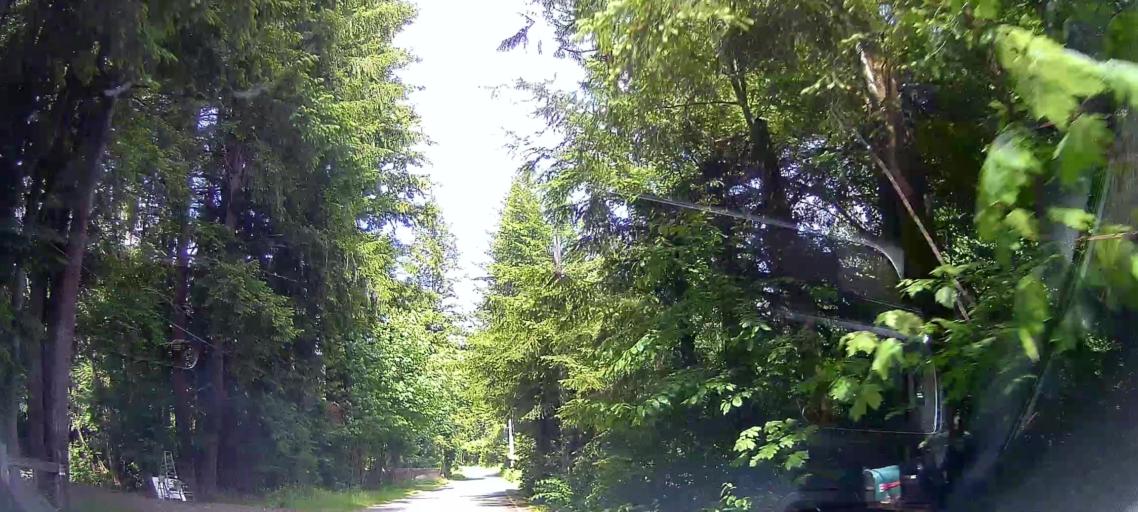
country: US
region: Washington
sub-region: Whatcom County
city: Sudden Valley
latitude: 48.6788
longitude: -122.1849
